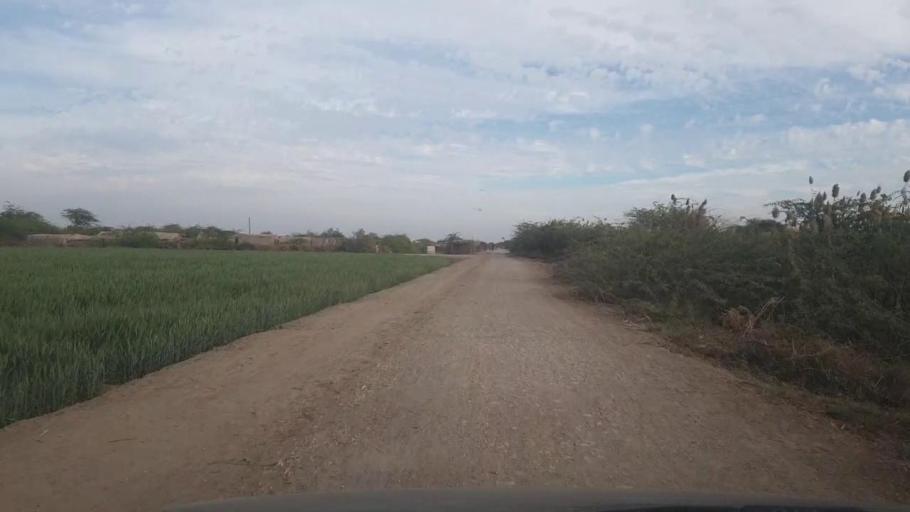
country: PK
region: Sindh
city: Samaro
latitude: 25.3300
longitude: 69.2601
